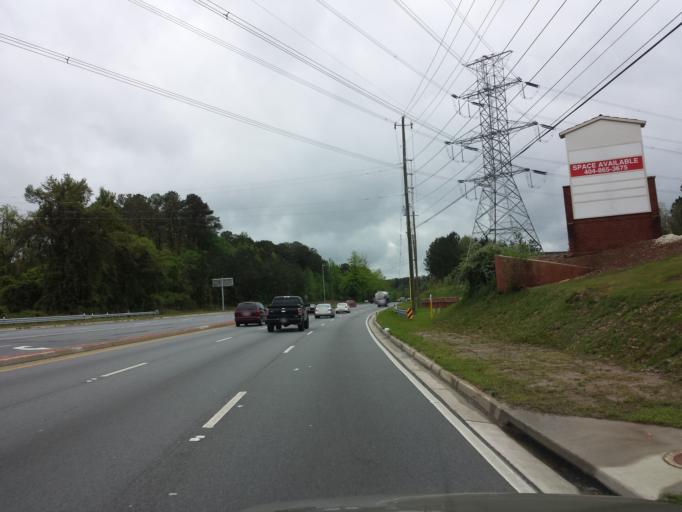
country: US
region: Georgia
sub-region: Cobb County
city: Kennesaw
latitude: 33.9920
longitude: -84.5984
